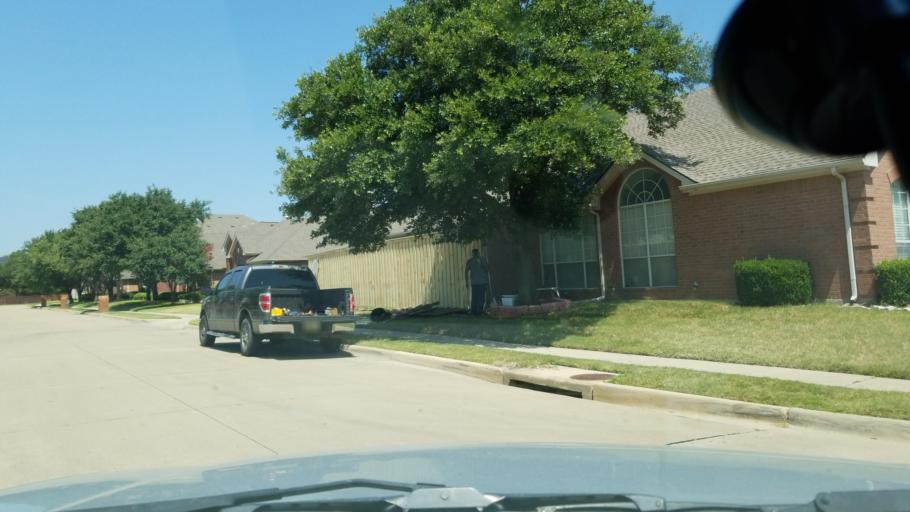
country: US
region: Texas
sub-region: Dallas County
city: Farmers Branch
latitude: 32.9293
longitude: -96.9438
